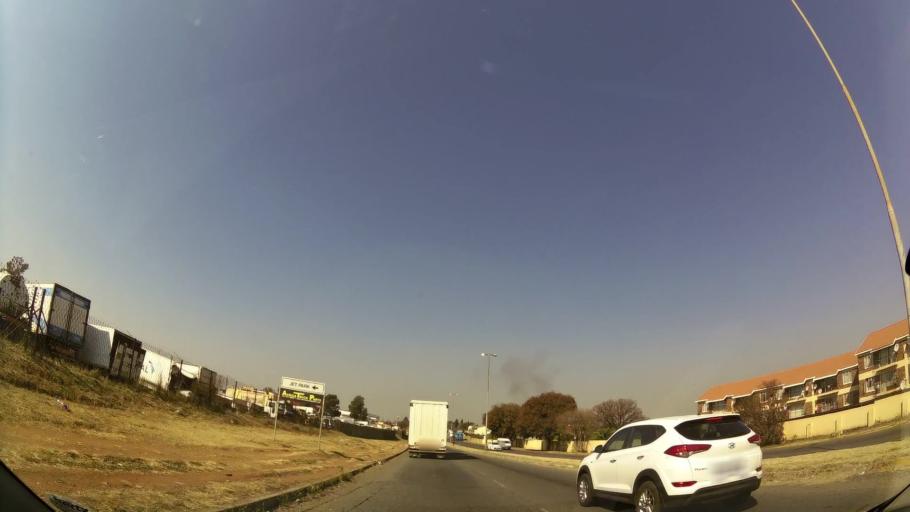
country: ZA
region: Gauteng
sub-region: Ekurhuleni Metropolitan Municipality
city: Boksburg
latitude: -26.1737
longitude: 28.2089
